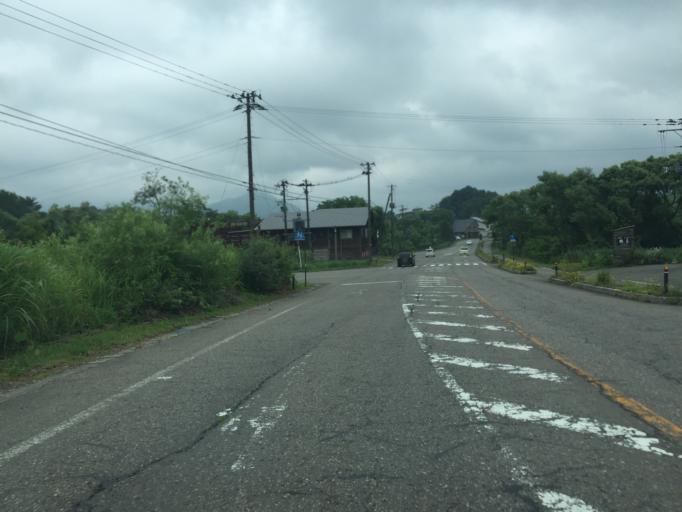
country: JP
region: Fukushima
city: Inawashiro
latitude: 37.6645
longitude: 140.0802
